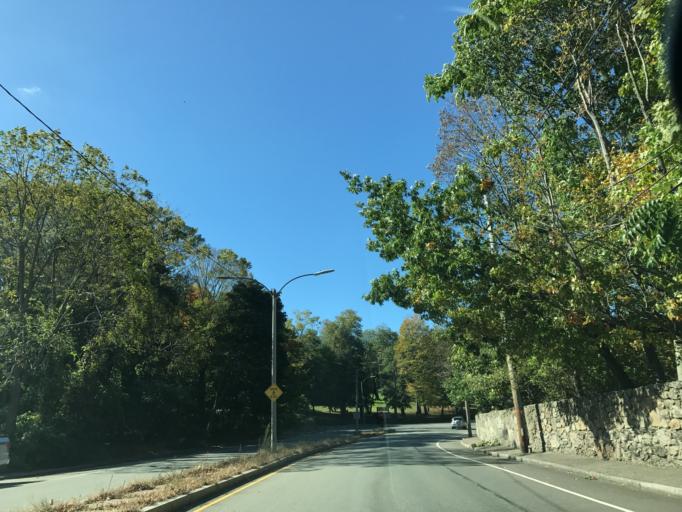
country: US
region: Massachusetts
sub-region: Suffolk County
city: Jamaica Plain
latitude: 42.3191
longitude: -71.1246
